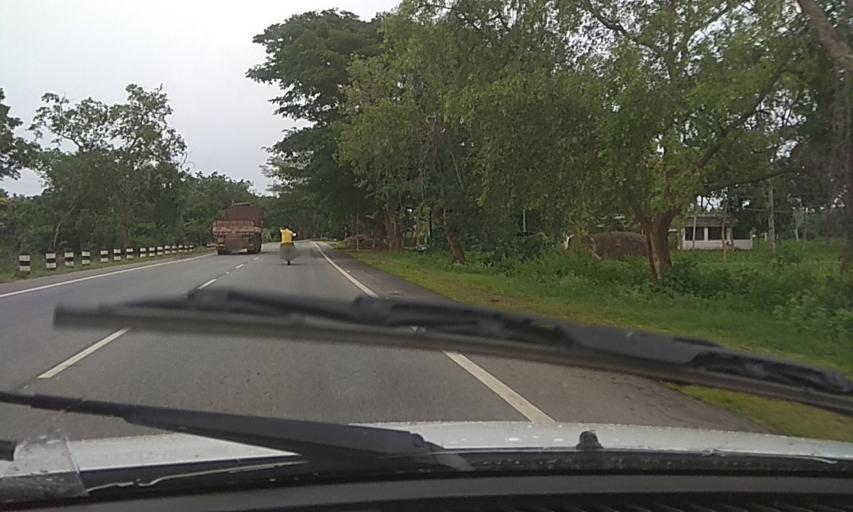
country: IN
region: Karnataka
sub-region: Mandya
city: Maddur
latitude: 12.7948
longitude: 77.0436
